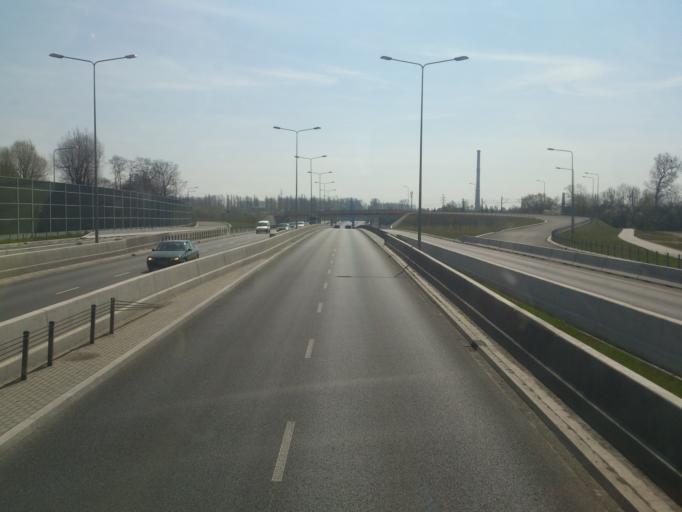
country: PL
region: Lodz Voivodeship
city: Lodz
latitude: 51.7253
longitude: 19.4496
